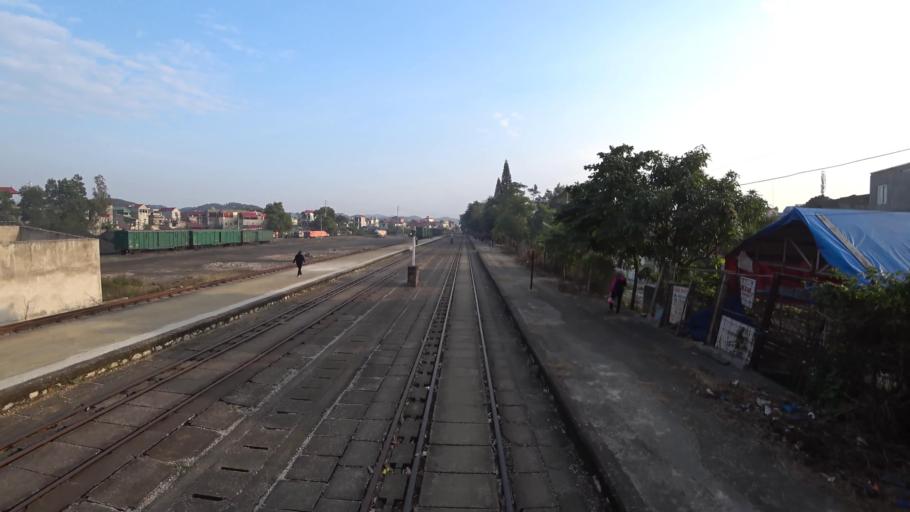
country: VN
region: Lang Son
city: Thi Tran Cao Loc
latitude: 21.8663
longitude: 106.7635
